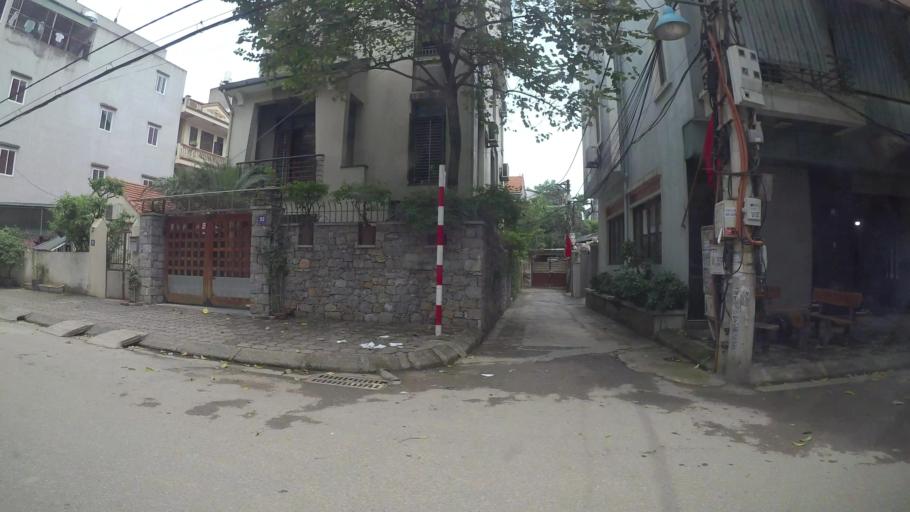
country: VN
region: Ha Noi
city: Tay Ho
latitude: 21.0886
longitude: 105.7956
